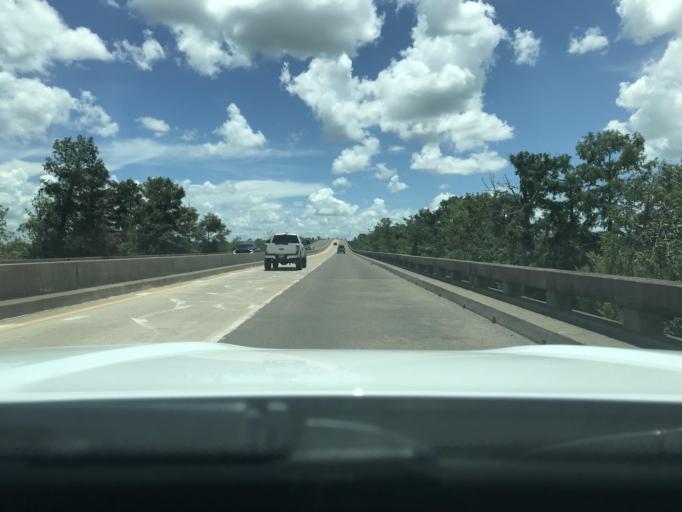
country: US
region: Louisiana
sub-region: Calcasieu Parish
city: Moss Bluff
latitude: 30.2910
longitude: -93.1919
